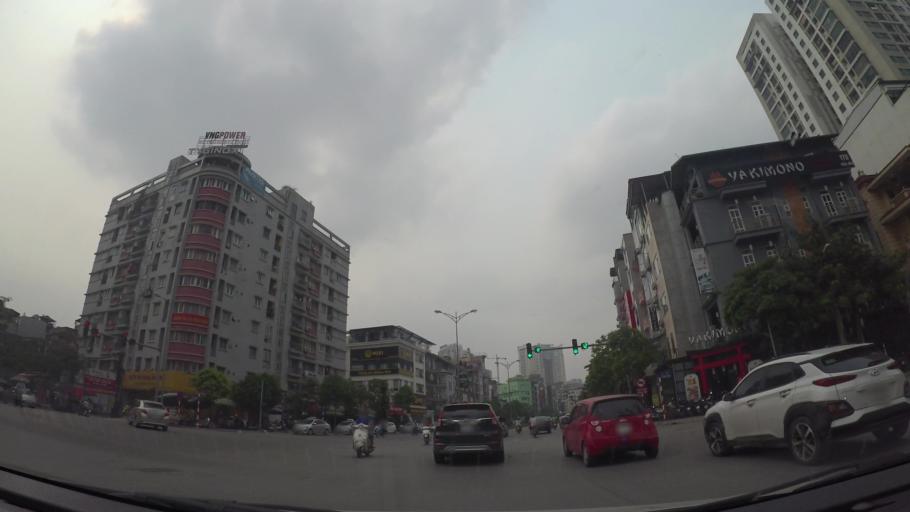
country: VN
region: Ha Noi
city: Cau Dien
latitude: 21.0299
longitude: 105.7754
